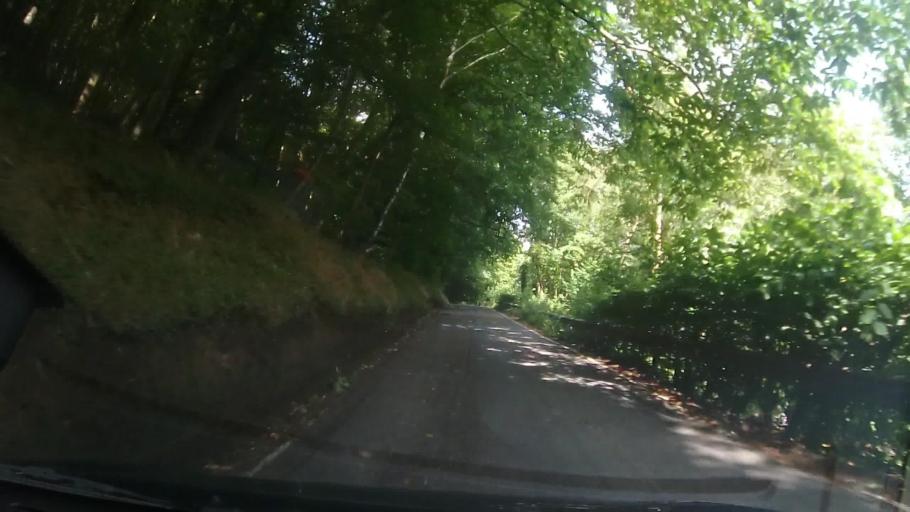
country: GB
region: Wales
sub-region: Sir Powys
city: Knighton
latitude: 52.3461
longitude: -3.0368
